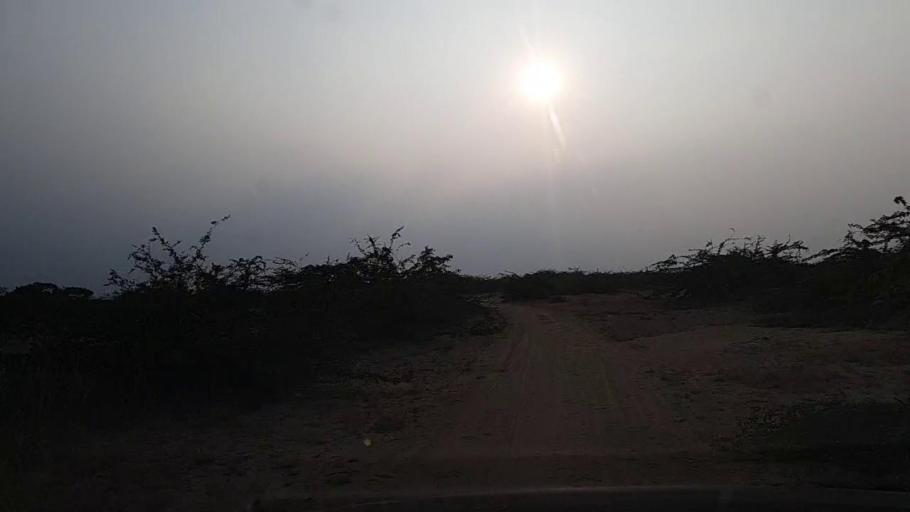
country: PK
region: Sindh
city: Gharo
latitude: 24.7796
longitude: 67.7095
